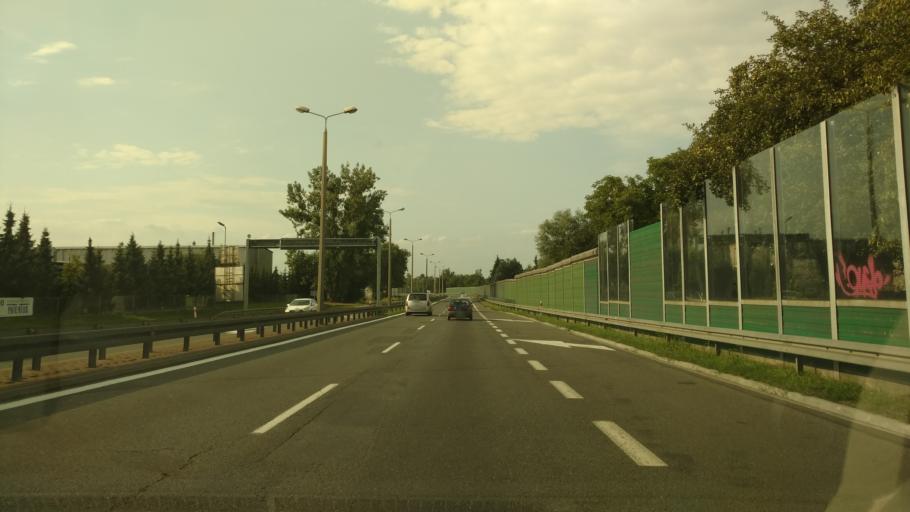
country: PL
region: Silesian Voivodeship
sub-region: Powiat pszczynski
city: Pszczyna
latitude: 49.9771
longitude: 18.9588
